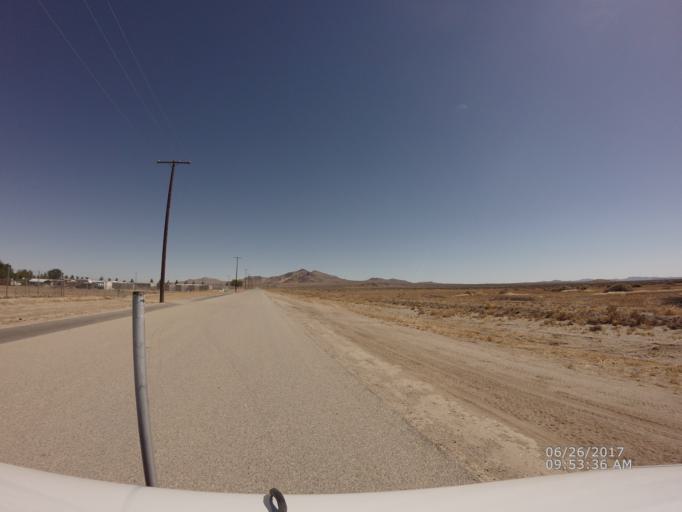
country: US
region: California
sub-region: Los Angeles County
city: Lake Los Angeles
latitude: 34.6290
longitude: -117.8095
